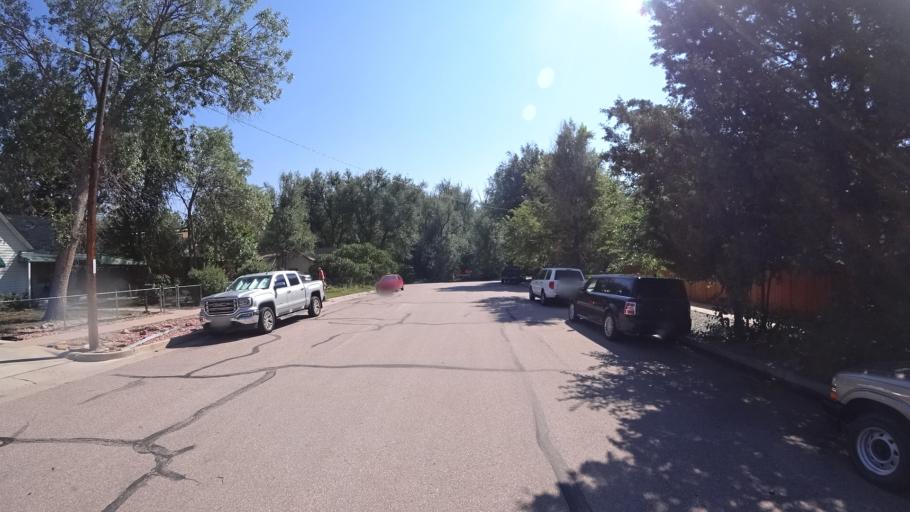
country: US
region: Colorado
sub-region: El Paso County
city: Colorado Springs
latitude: 38.8431
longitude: -104.8136
